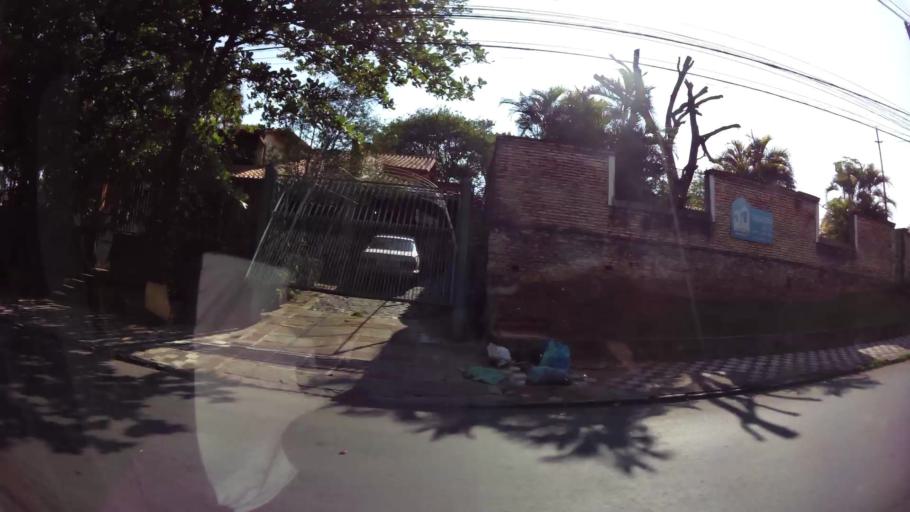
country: PY
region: Asuncion
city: Asuncion
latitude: -25.3097
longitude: -57.6316
